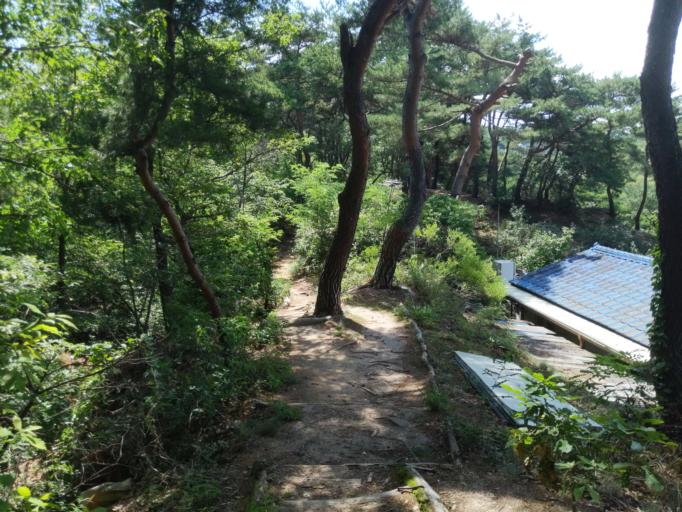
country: KR
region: Seoul
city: Seoul
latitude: 37.6026
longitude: 126.9650
